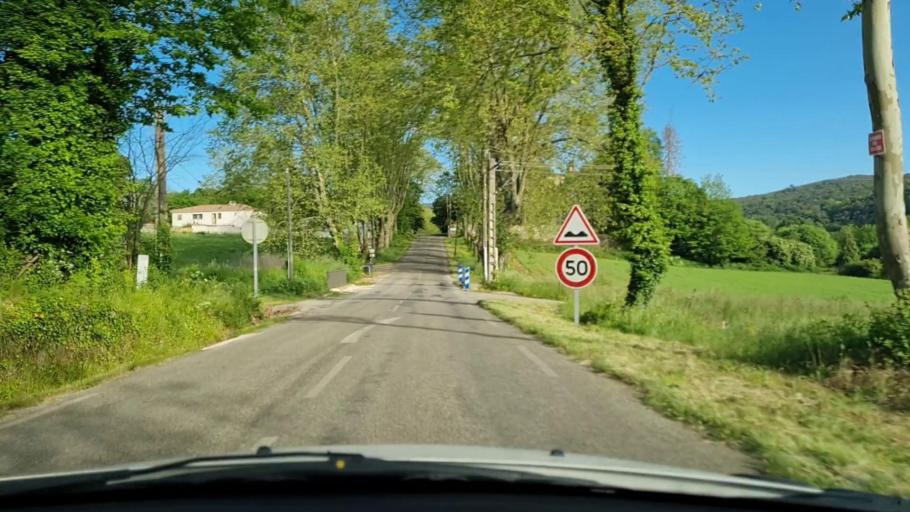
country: FR
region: Languedoc-Roussillon
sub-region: Departement du Gard
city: Cendras
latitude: 44.1503
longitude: 4.0471
